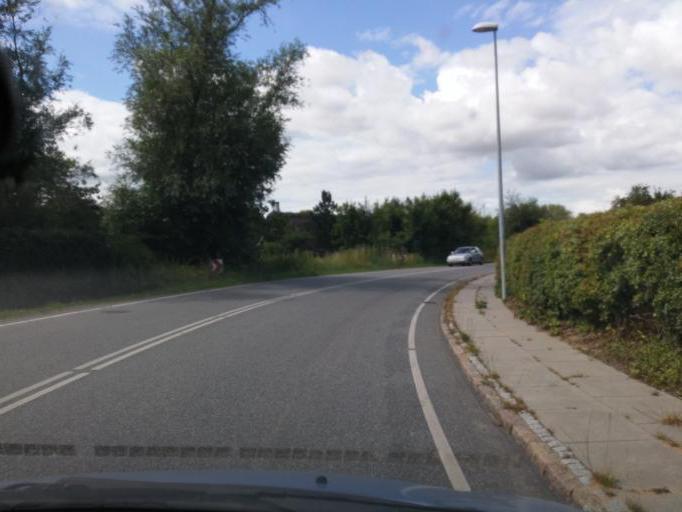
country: DK
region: South Denmark
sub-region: Kerteminde Kommune
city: Langeskov
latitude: 55.4053
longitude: 10.5867
